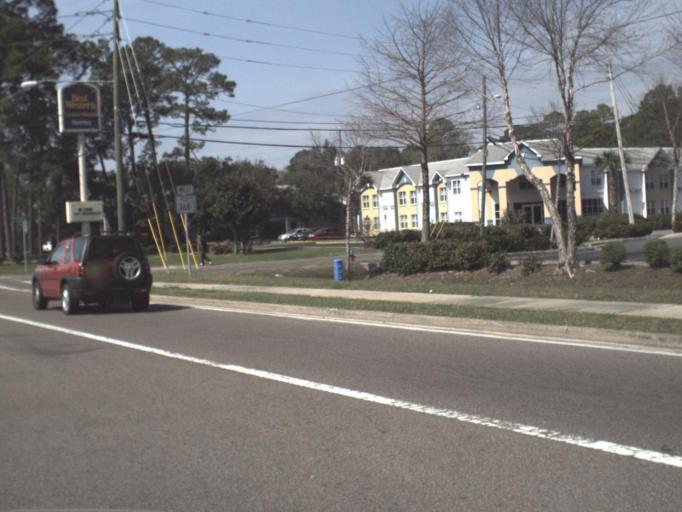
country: US
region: Florida
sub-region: Bay County
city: Hiland Park
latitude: 30.1895
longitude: -85.6411
